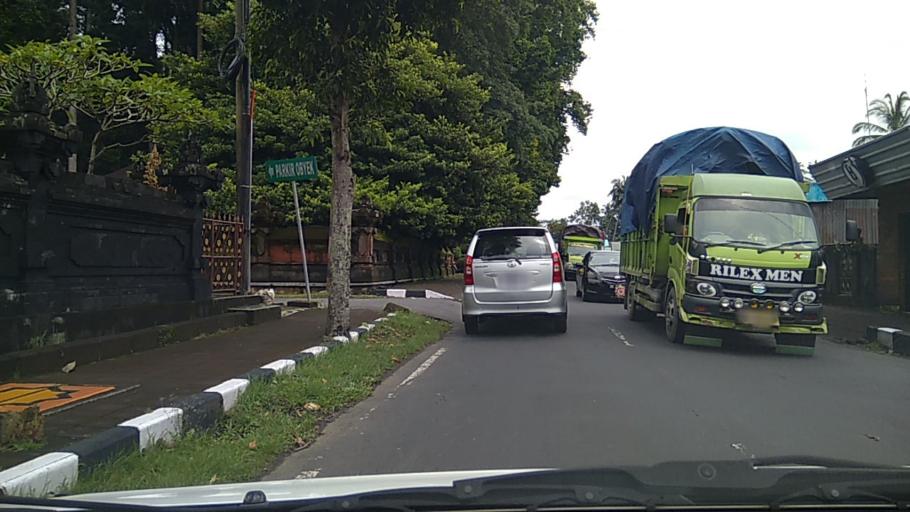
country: ID
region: Bali
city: Brahmana
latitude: -8.4814
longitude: 115.2092
